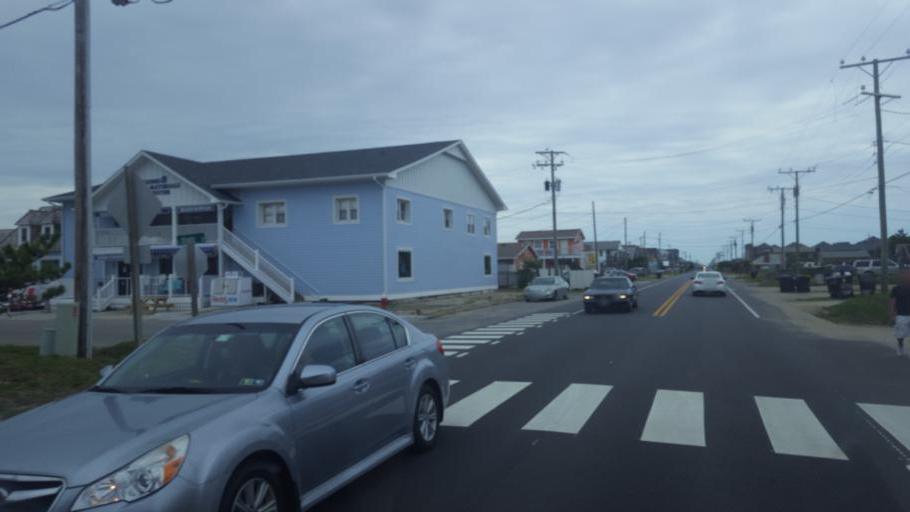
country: US
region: North Carolina
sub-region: Dare County
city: Kill Devil Hills
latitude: 36.0029
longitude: -75.6506
